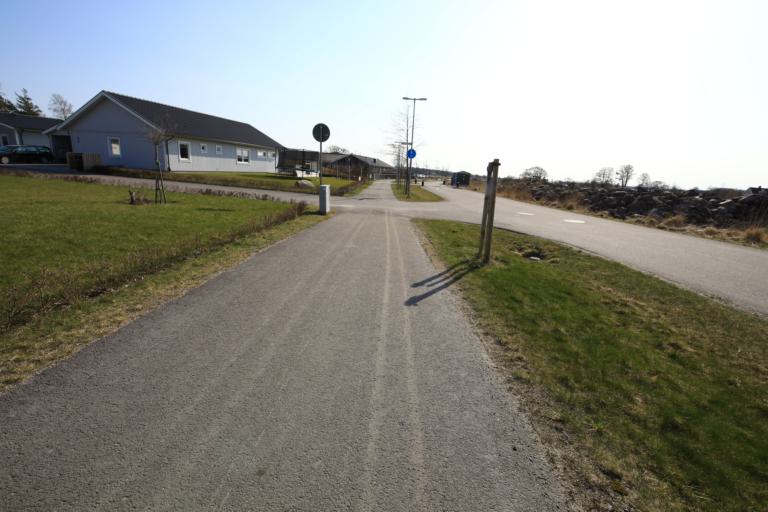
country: SE
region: Halland
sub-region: Varbergs Kommun
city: Varberg
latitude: 57.1459
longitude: 12.2793
